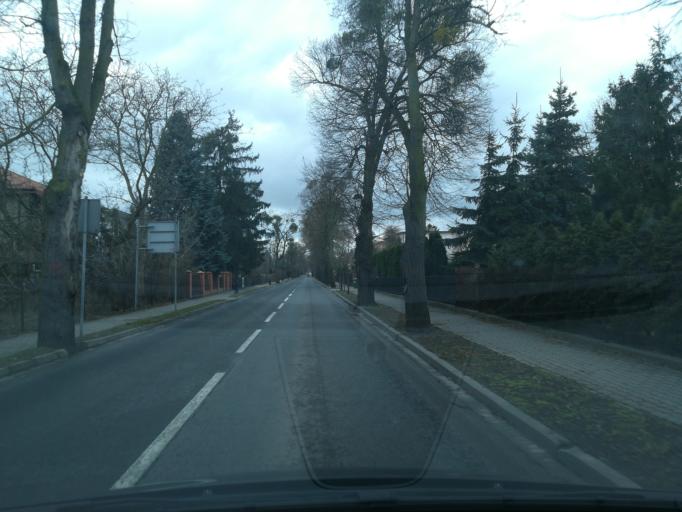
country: PL
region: Kujawsko-Pomorskie
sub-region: Powiat aleksandrowski
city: Ciechocinek
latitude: 52.8778
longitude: 18.7812
